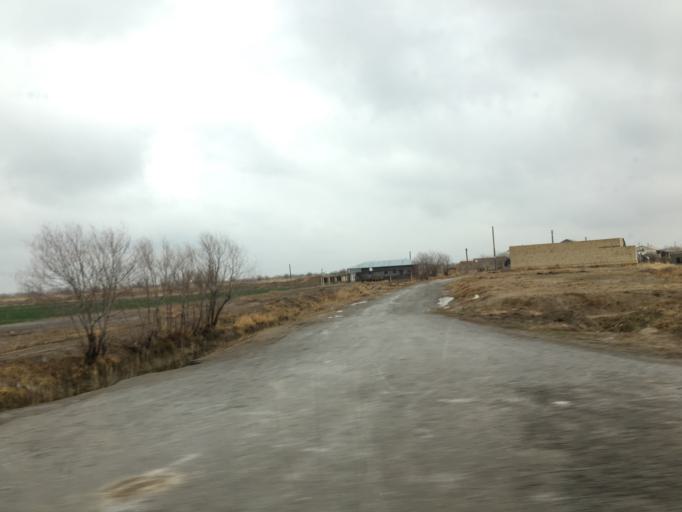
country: TM
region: Mary
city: Yoloeten
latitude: 37.3108
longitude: 62.3191
